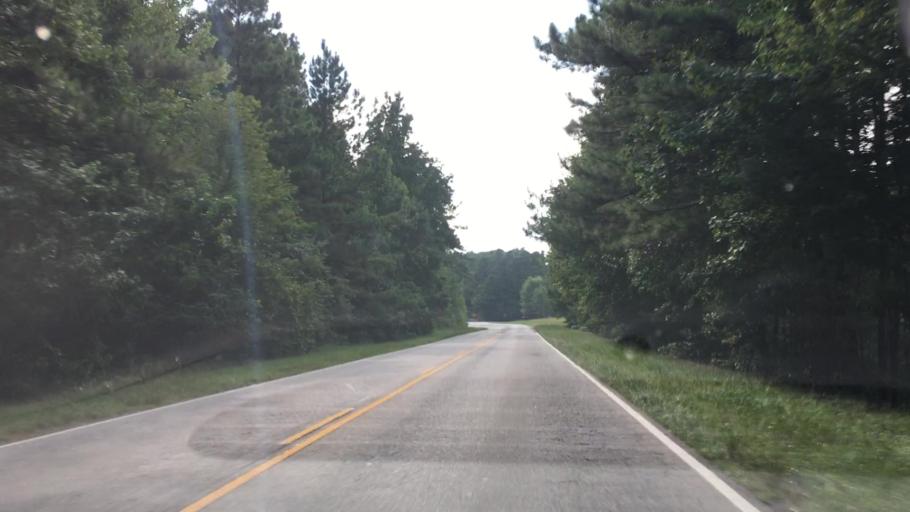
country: US
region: South Carolina
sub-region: Aiken County
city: Aiken
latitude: 33.5269
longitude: -81.7390
